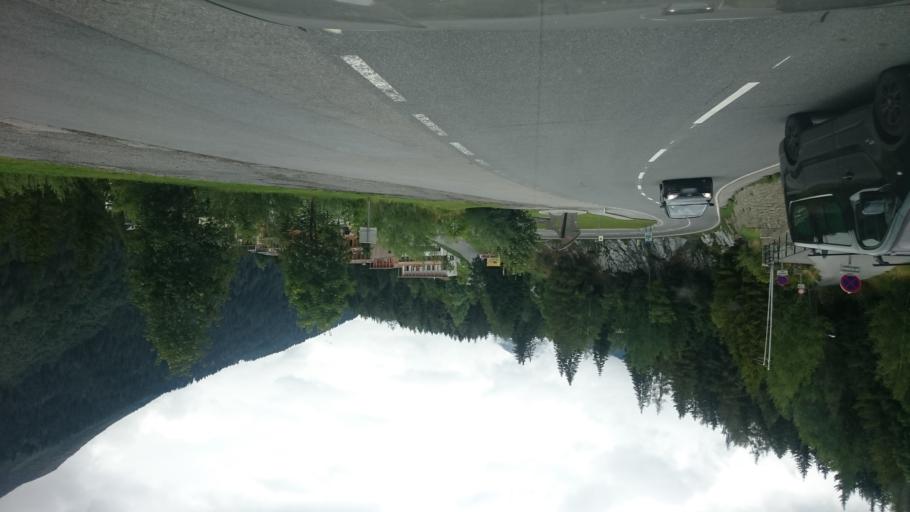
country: AT
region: Tyrol
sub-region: Politischer Bezirk Landeck
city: Sankt Anton am Arlberg
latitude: 47.1240
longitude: 10.2485
